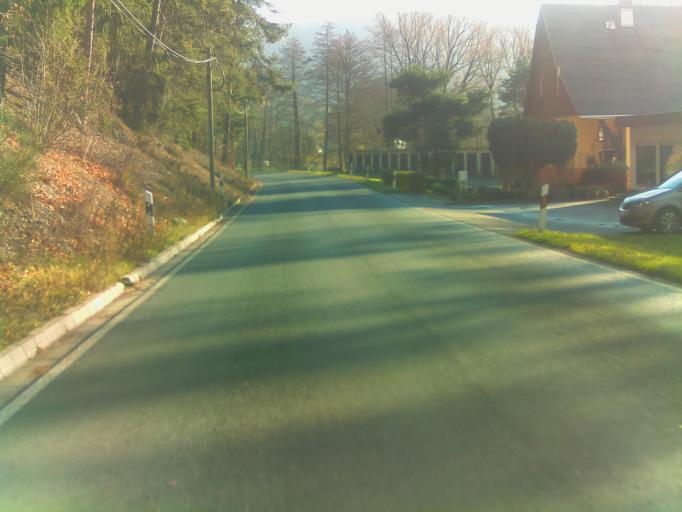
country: DE
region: Thuringia
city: Mellenbach-Glasbach
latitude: 50.6095
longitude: 11.1199
